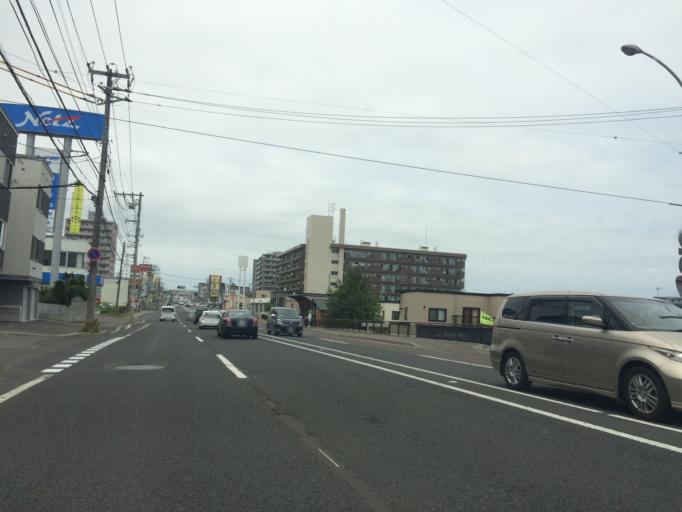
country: JP
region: Hokkaido
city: Sapporo
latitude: 43.1050
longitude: 141.2514
